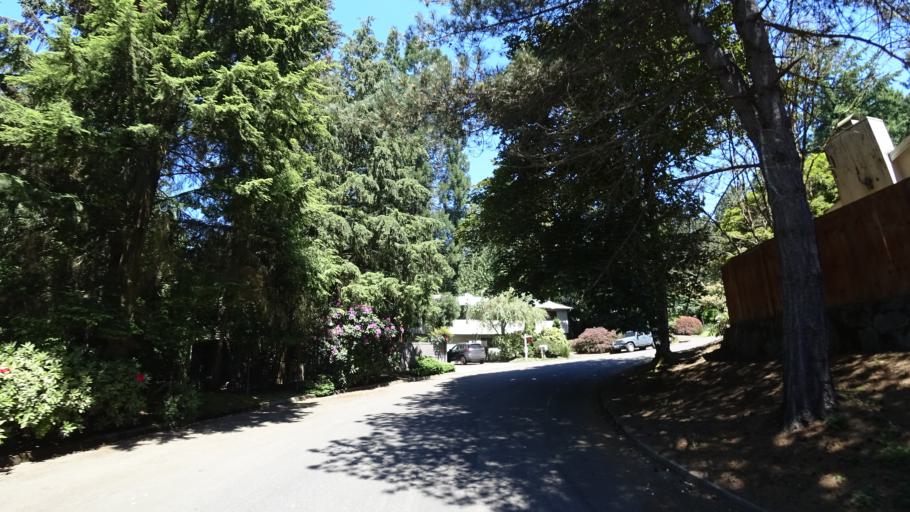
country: US
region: Oregon
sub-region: Washington County
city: Raleigh Hills
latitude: 45.4945
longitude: -122.7232
